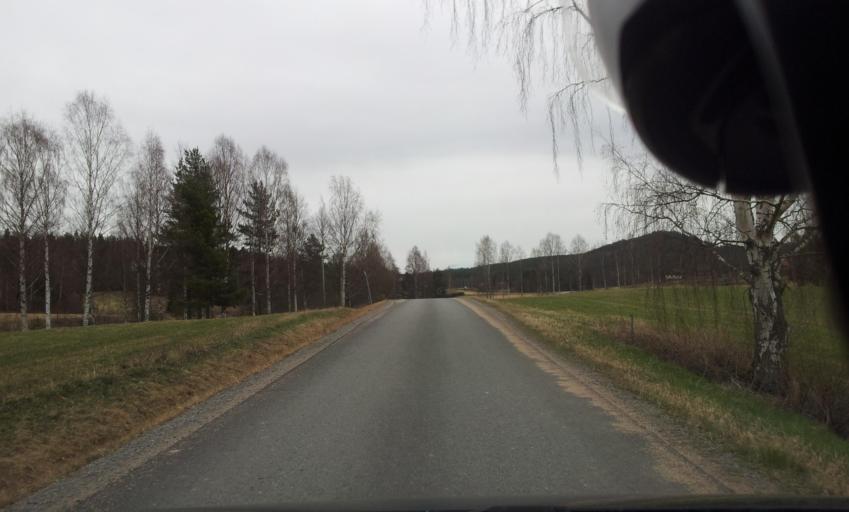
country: SE
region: Gaevleborg
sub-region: Ljusdals Kommun
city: Farila
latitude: 61.7992
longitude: 15.9158
